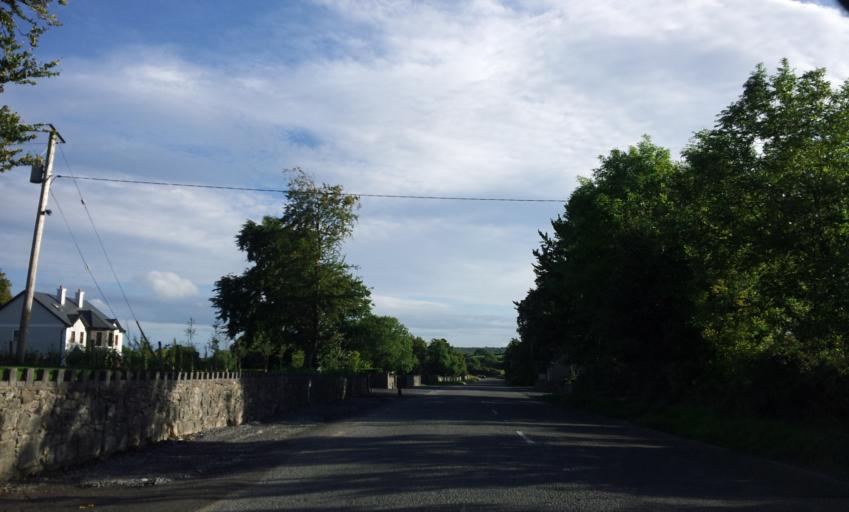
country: IE
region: Munster
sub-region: An Clar
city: Ennis
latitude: 52.8881
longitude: -9.0324
